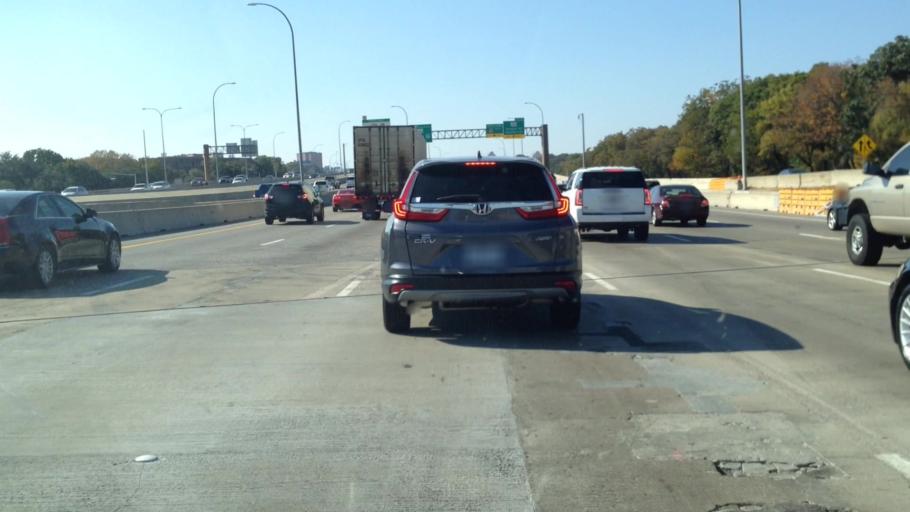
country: US
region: Texas
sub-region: Dallas County
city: Richardson
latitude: 32.9252
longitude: -96.7818
